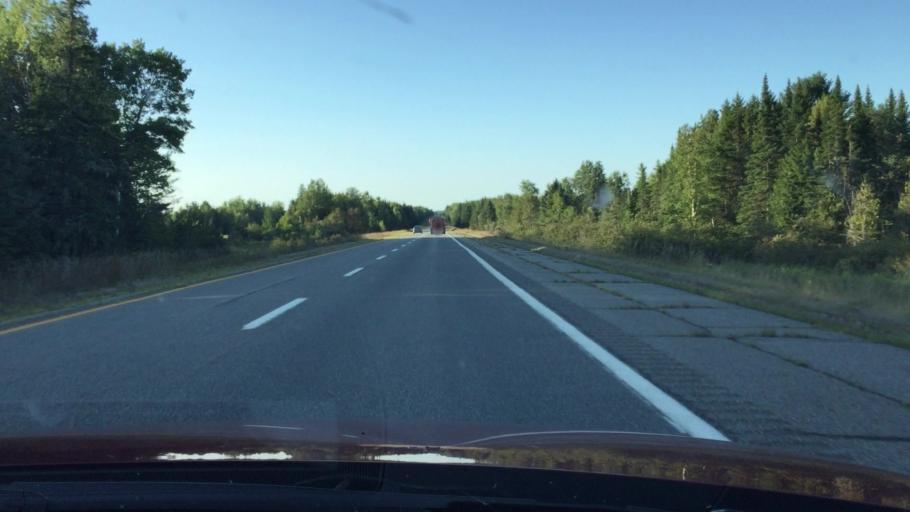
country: US
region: Maine
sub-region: Penobscot County
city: Patten
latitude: 45.8181
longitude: -68.4298
